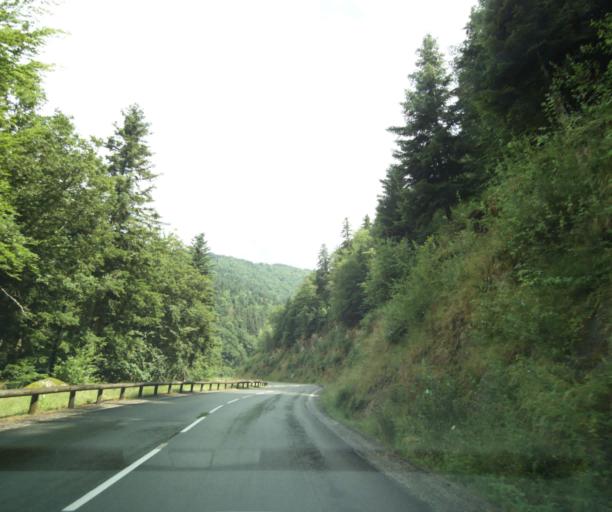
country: FR
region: Auvergne
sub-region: Departement de la Haute-Loire
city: Saugues
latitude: 44.9576
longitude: 3.6276
